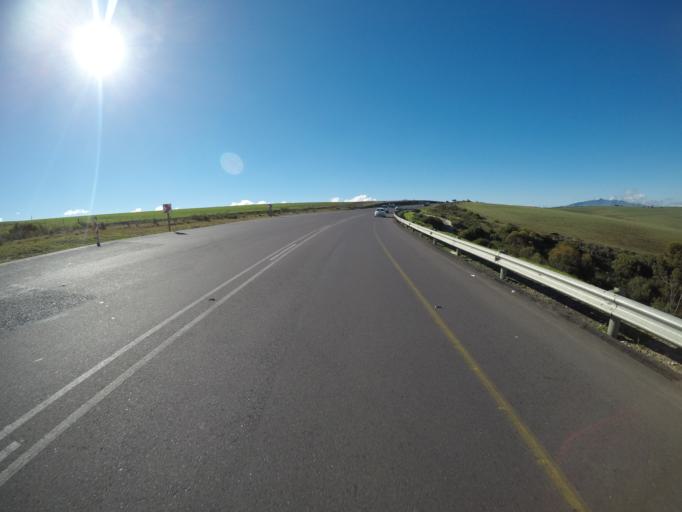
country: ZA
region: Western Cape
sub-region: Overberg District Municipality
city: Caledon
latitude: -34.2264
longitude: 19.2733
